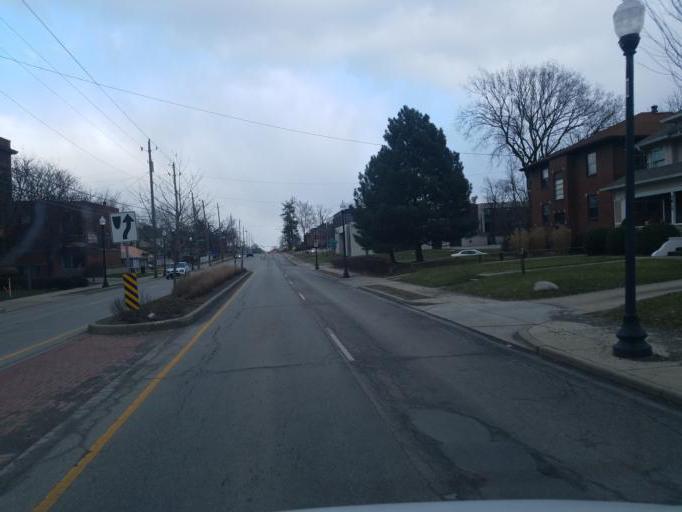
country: US
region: Indiana
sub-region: Marion County
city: Warren Park
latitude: 39.7708
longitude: -86.0681
